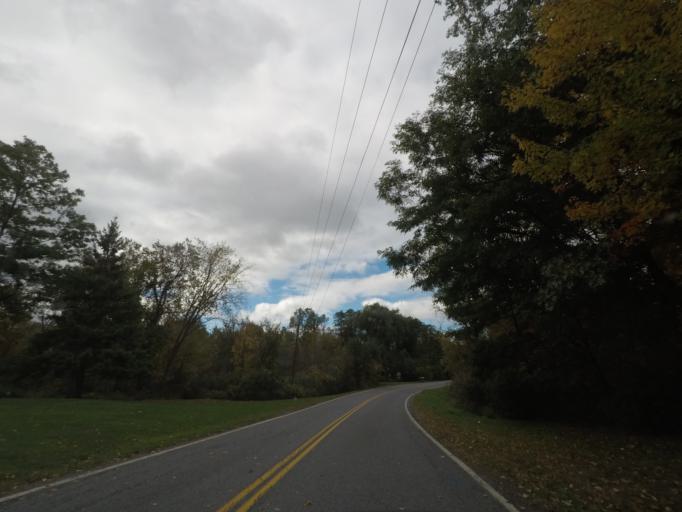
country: US
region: New York
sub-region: Saratoga County
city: Mechanicville
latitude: 42.8816
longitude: -73.7441
